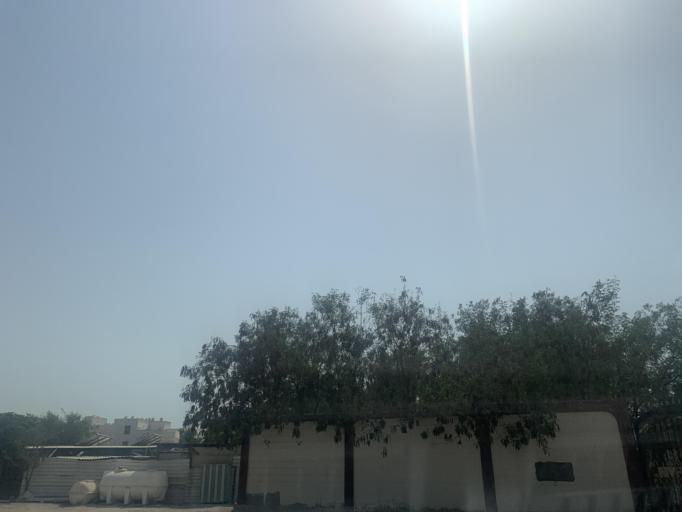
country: BH
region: Manama
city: Jidd Hafs
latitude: 26.2096
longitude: 50.4645
